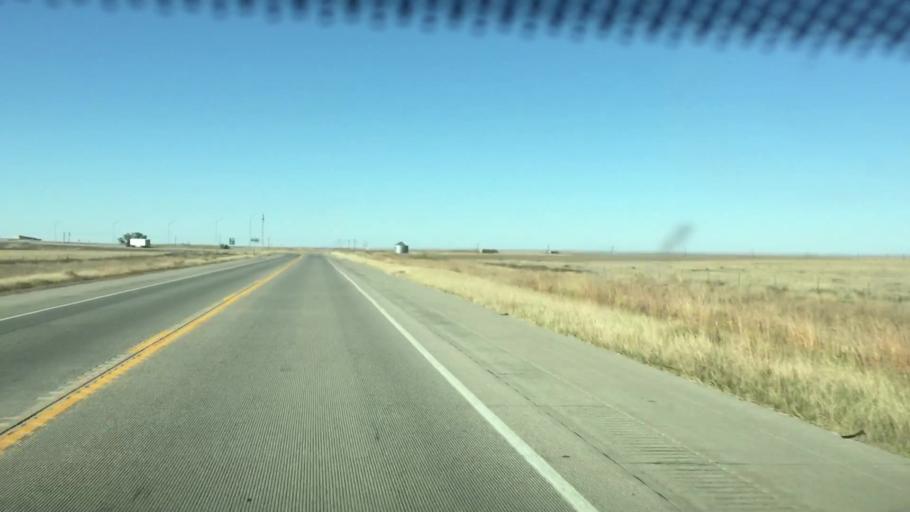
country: US
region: Colorado
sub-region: Kiowa County
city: Eads
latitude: 38.7572
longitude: -102.7769
